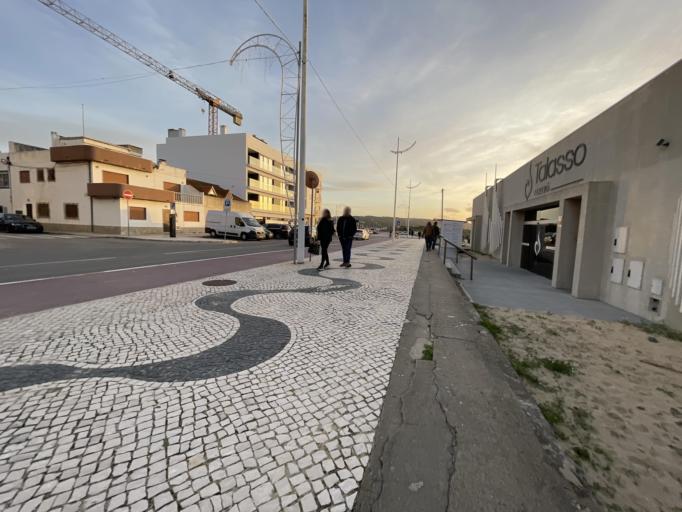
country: PT
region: Leiria
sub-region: Nazare
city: Nazare
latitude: 39.5909
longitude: -9.0738
